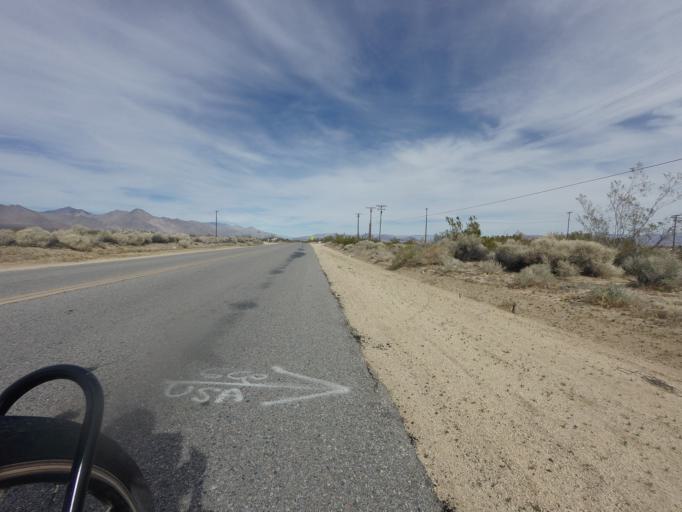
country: US
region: California
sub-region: Kern County
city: Inyokern
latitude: 35.7096
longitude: -117.8313
